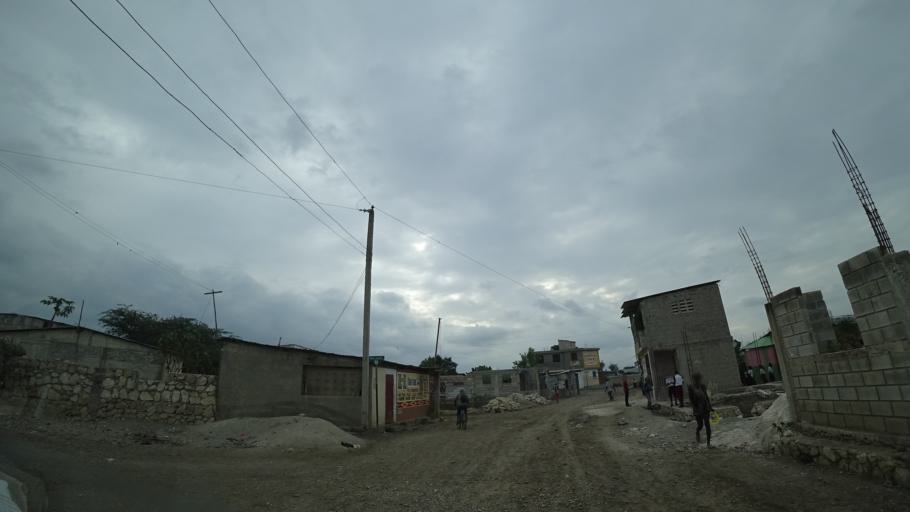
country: HT
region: Ouest
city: Croix des Bouquets
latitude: 18.6472
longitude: -72.2756
